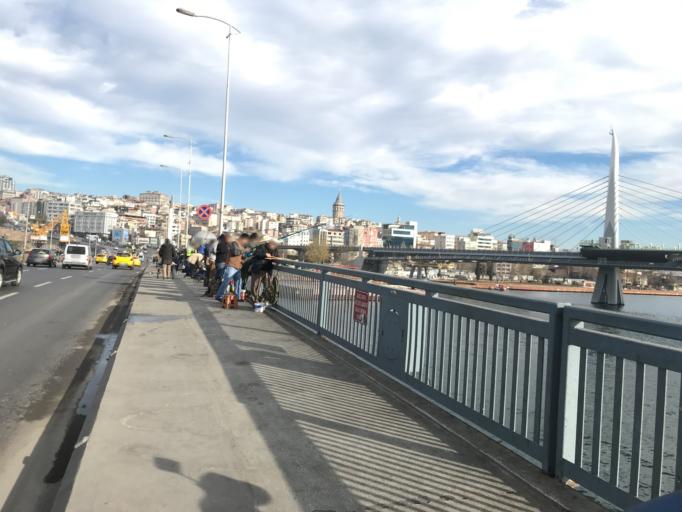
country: TR
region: Istanbul
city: Eminoenue
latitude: 41.0239
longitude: 28.9648
